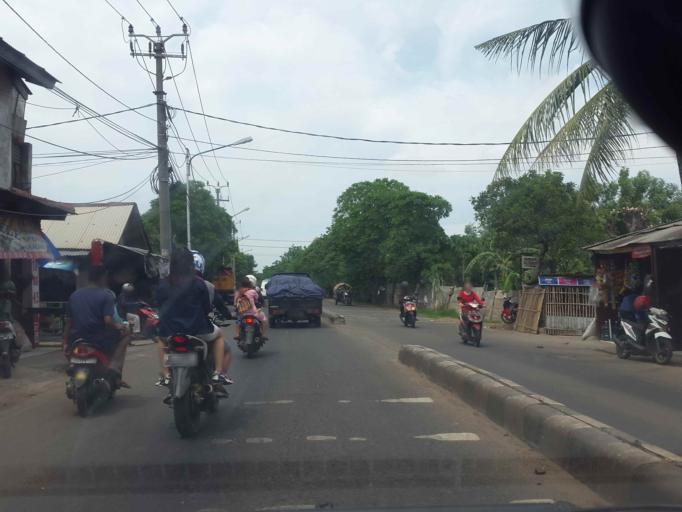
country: ID
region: Banten
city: Tangerang
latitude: -6.1579
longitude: 106.6419
